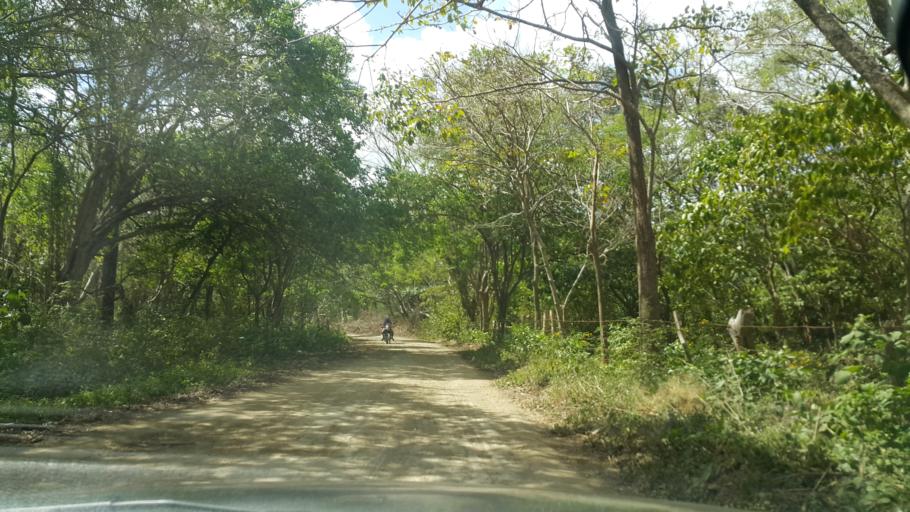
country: NI
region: Rivas
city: San Juan del Sur
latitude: 11.3138
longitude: -85.8451
